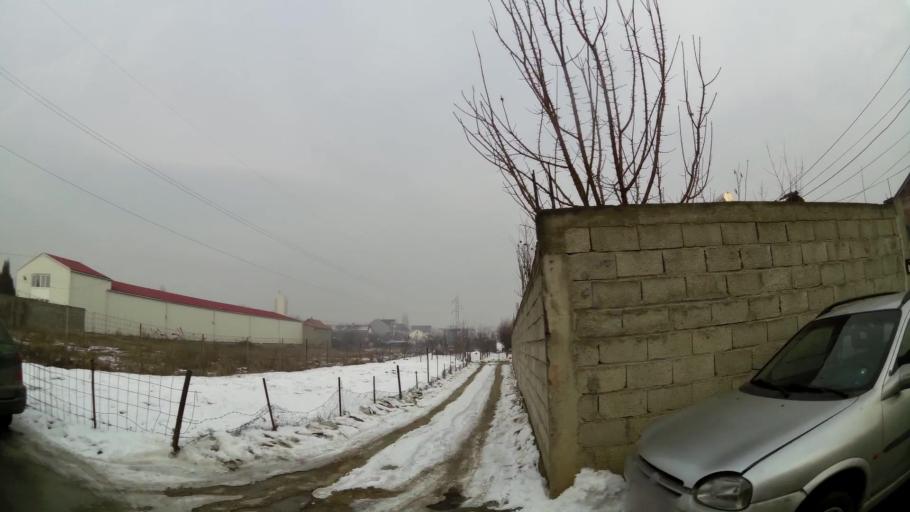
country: MK
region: Suto Orizari
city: Suto Orizare
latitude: 42.0289
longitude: 21.4246
